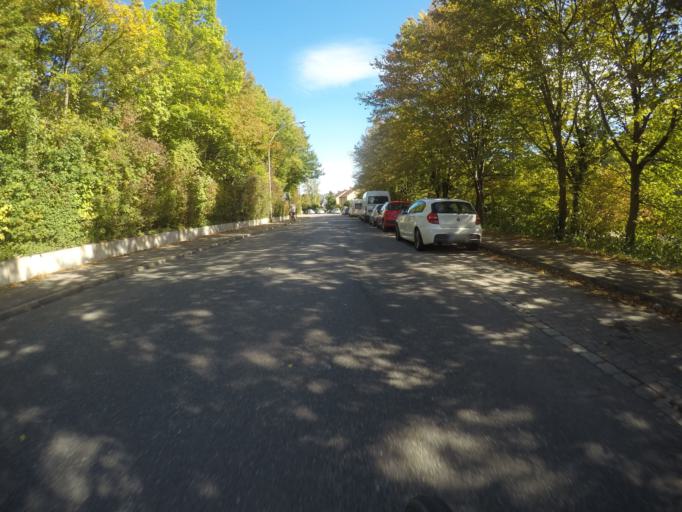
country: DE
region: Baden-Wuerttemberg
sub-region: Regierungsbezirk Stuttgart
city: Ostfildern
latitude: 48.7583
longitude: 9.2386
